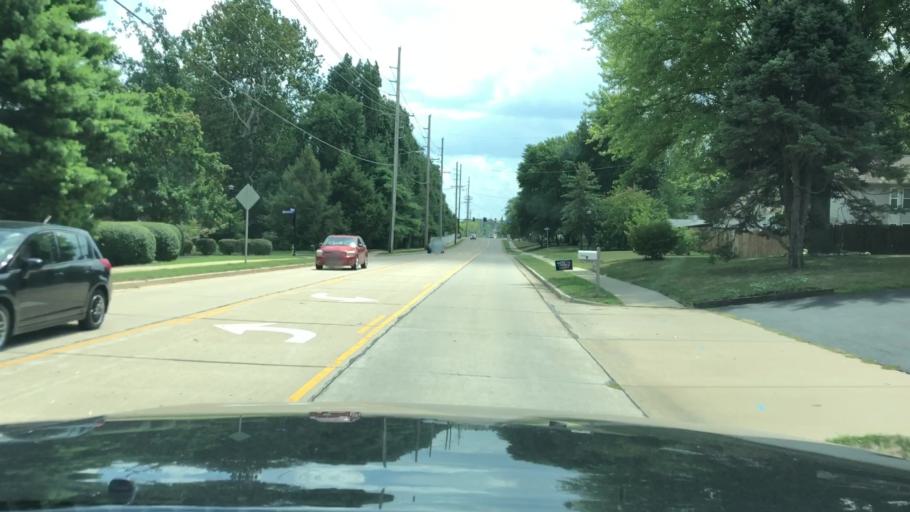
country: US
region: Missouri
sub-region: Saint Charles County
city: Saint Charles
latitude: 38.8056
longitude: -90.5355
